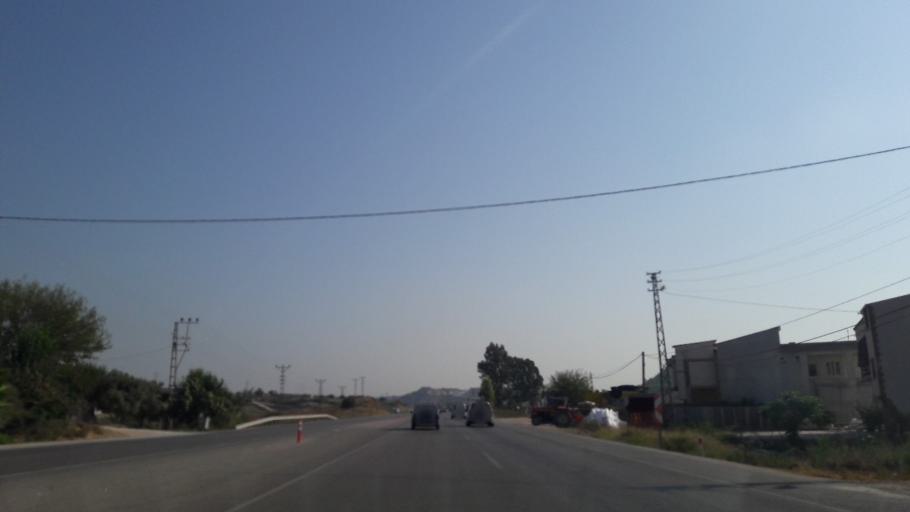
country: TR
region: Adana
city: Yuregir
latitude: 37.0667
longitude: 35.4503
